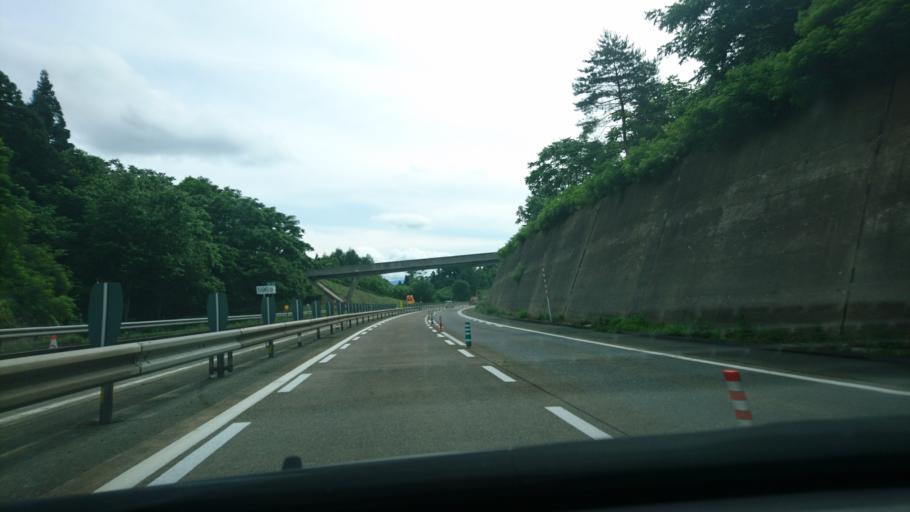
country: JP
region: Iwate
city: Ichinohe
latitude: 40.2264
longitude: 141.3682
